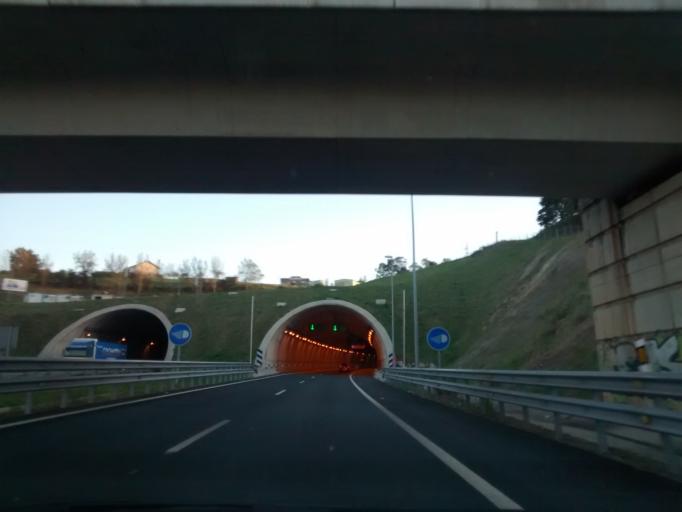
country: ES
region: Cantabria
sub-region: Provincia de Cantabria
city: Camargo
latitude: 43.3983
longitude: -3.8682
